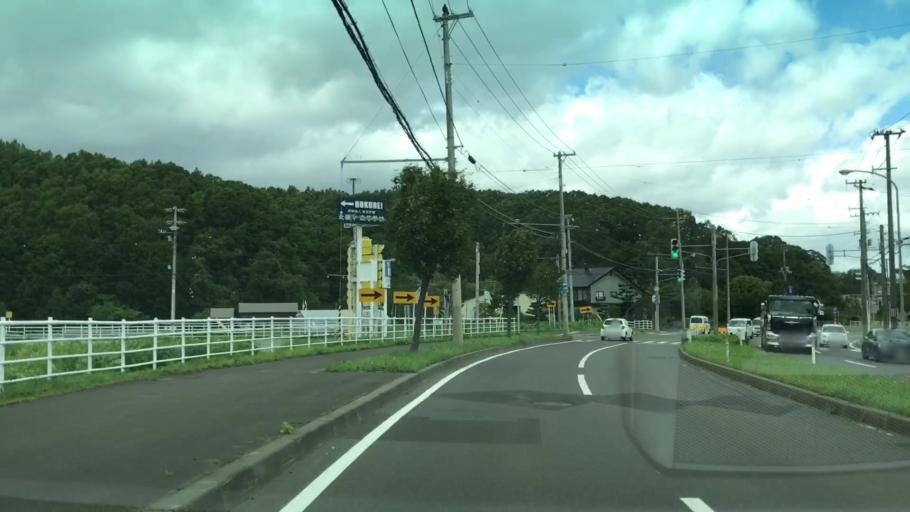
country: JP
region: Hokkaido
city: Sapporo
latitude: 42.9788
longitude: 141.4401
